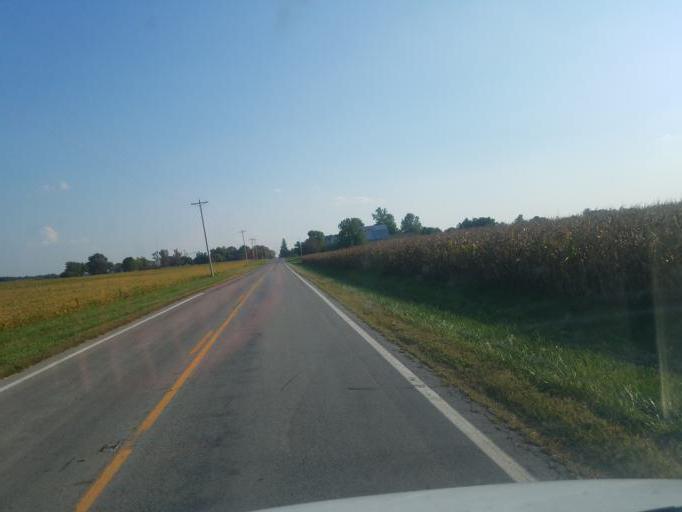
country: US
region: Ohio
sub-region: Wyandot County
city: Upper Sandusky
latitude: 40.9348
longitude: -83.1315
